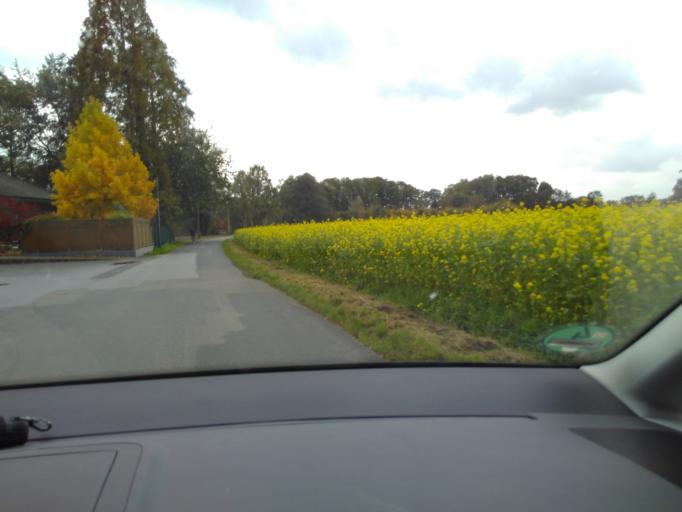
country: DE
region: North Rhine-Westphalia
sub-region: Regierungsbezirk Detmold
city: Verl
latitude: 51.8684
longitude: 8.4908
